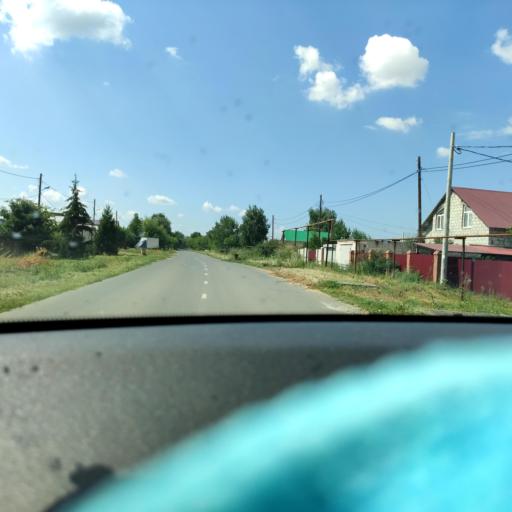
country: RU
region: Samara
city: Smyshlyayevka
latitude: 53.2197
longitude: 50.3354
